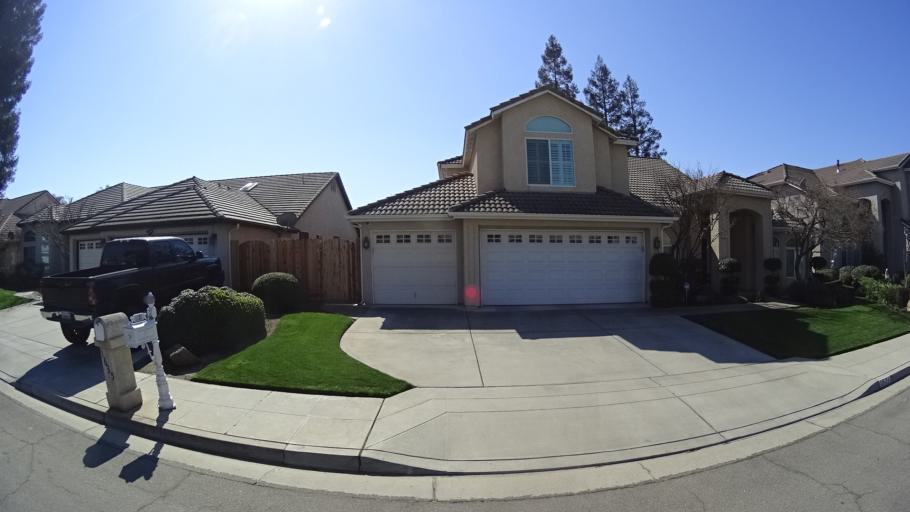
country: US
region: California
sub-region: Fresno County
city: Clovis
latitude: 36.8784
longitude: -119.7540
